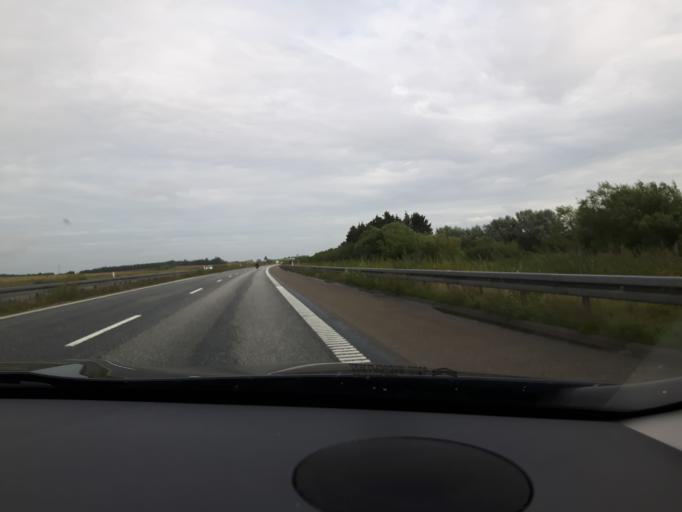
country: DK
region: North Denmark
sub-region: Hjorring Kommune
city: Vra
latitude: 57.3829
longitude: 10.0223
